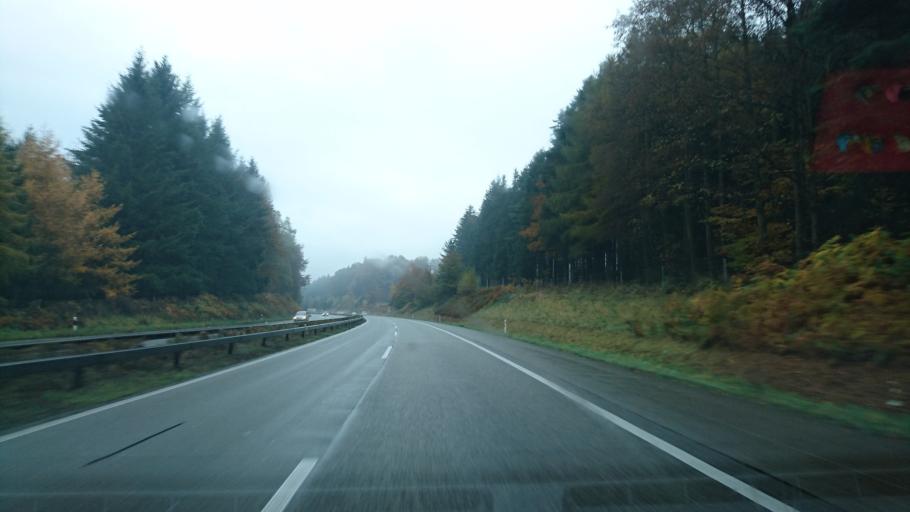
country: CH
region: Bern
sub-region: Bern-Mittelland District
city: Bariswil
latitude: 47.0285
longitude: 7.5248
